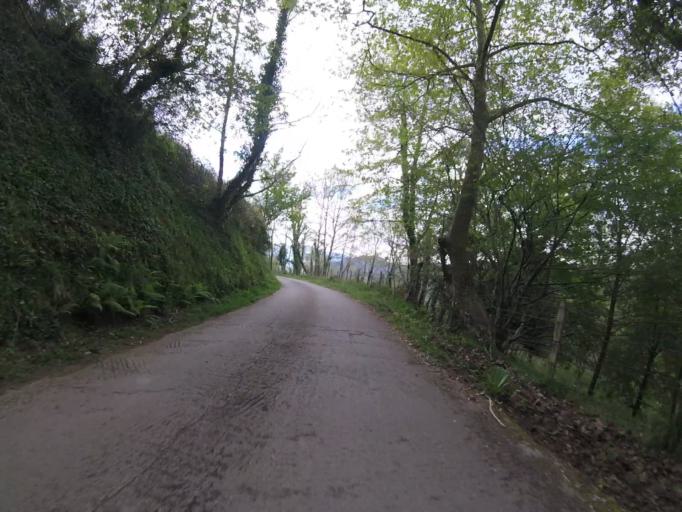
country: ES
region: Basque Country
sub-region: Provincia de Guipuzcoa
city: Aizarnazabal
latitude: 43.2540
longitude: -2.2149
